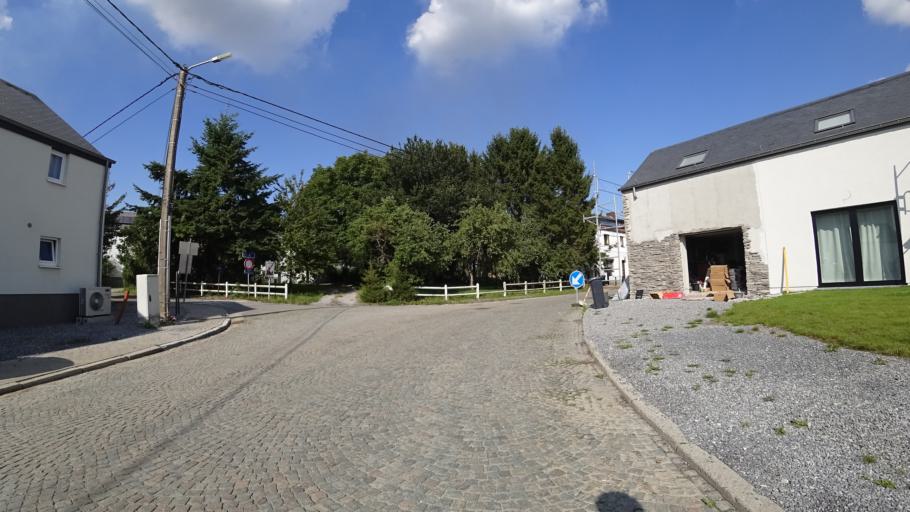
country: BE
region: Wallonia
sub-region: Province de Namur
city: Gembloux
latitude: 50.5059
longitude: 4.7281
